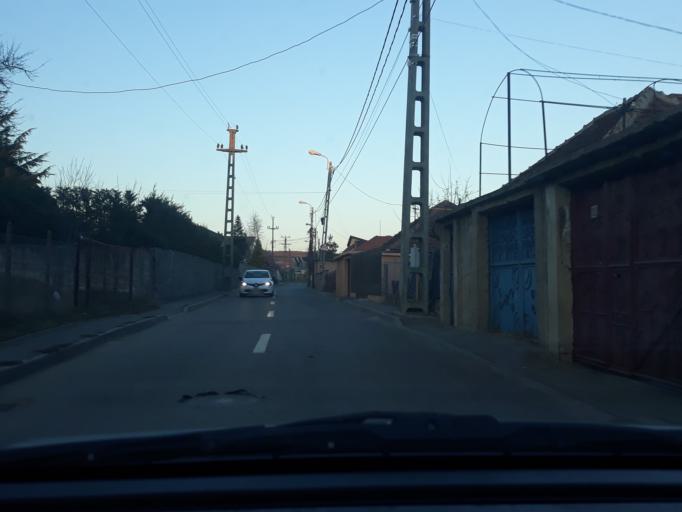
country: RO
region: Bihor
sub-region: Comuna Biharea
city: Oradea
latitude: 47.0790
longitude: 21.9436
